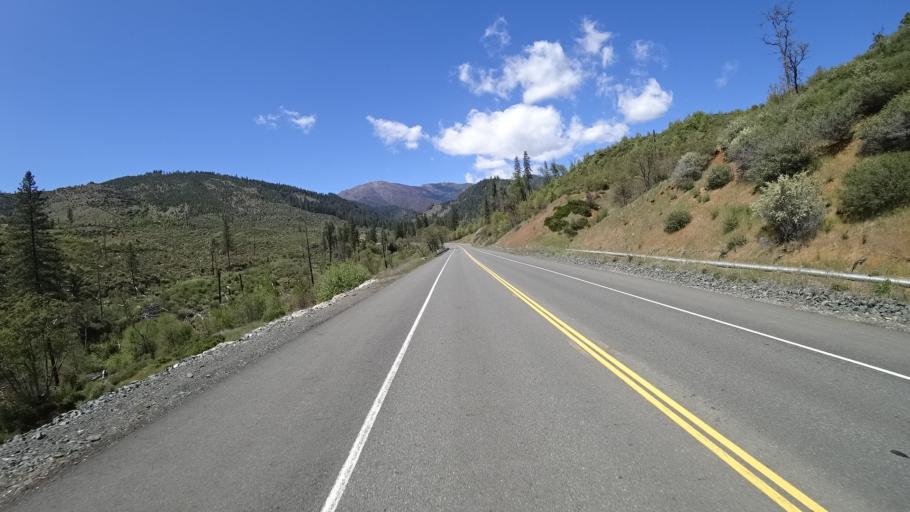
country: US
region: California
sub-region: Trinity County
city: Weaverville
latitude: 40.7396
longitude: -122.9670
